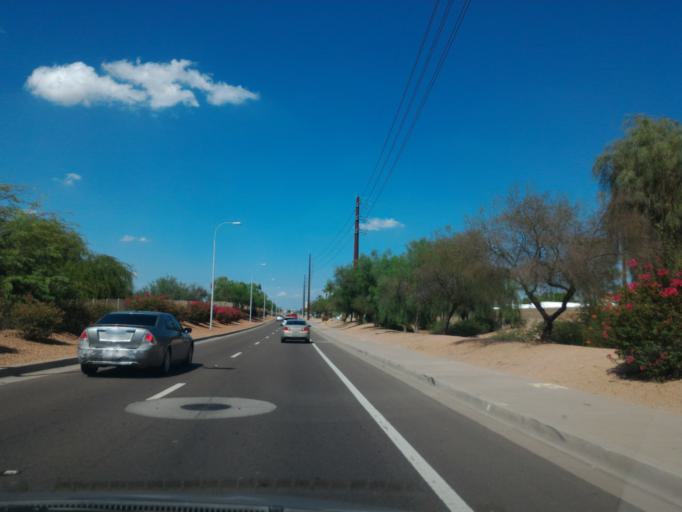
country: US
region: Arizona
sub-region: Maricopa County
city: Chandler
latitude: 33.2995
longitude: -111.8935
